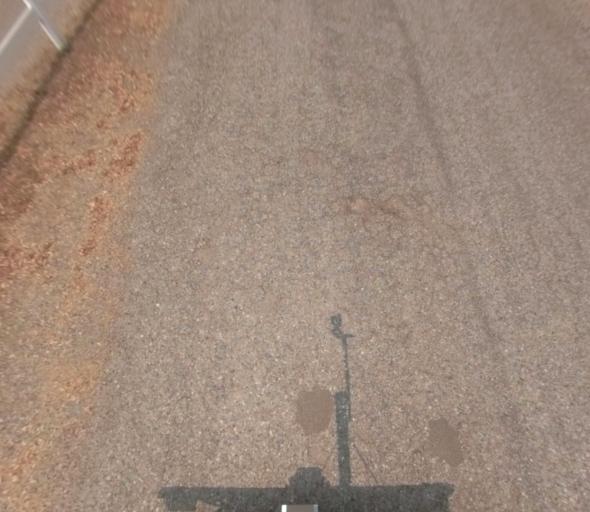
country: US
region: California
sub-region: Madera County
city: Coarsegold
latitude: 37.2672
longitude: -119.6856
